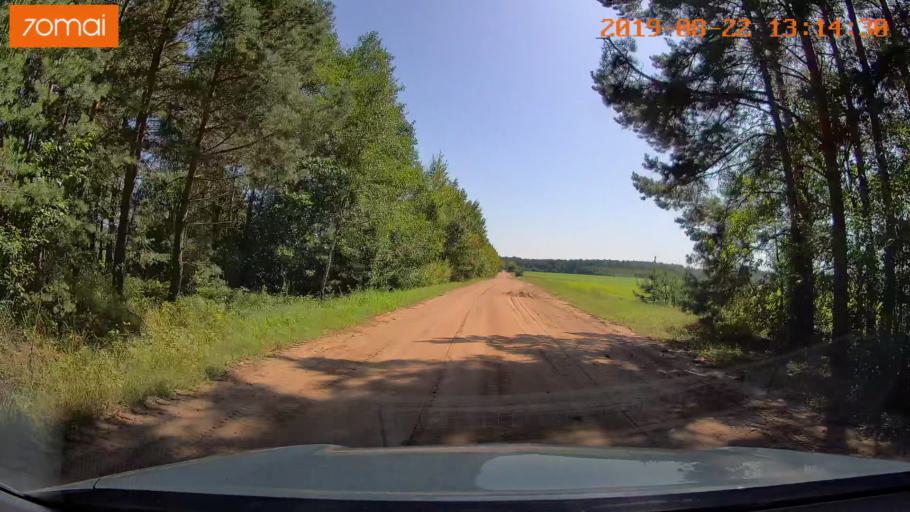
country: BY
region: Minsk
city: Prawdzinski
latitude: 53.2673
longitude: 27.8880
